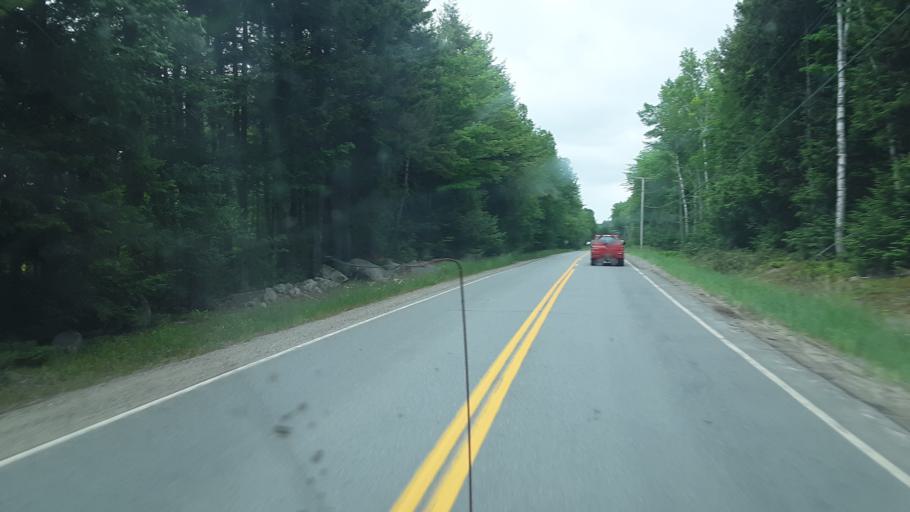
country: US
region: Maine
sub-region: Penobscot County
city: Millinocket
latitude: 45.6804
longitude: -68.7460
